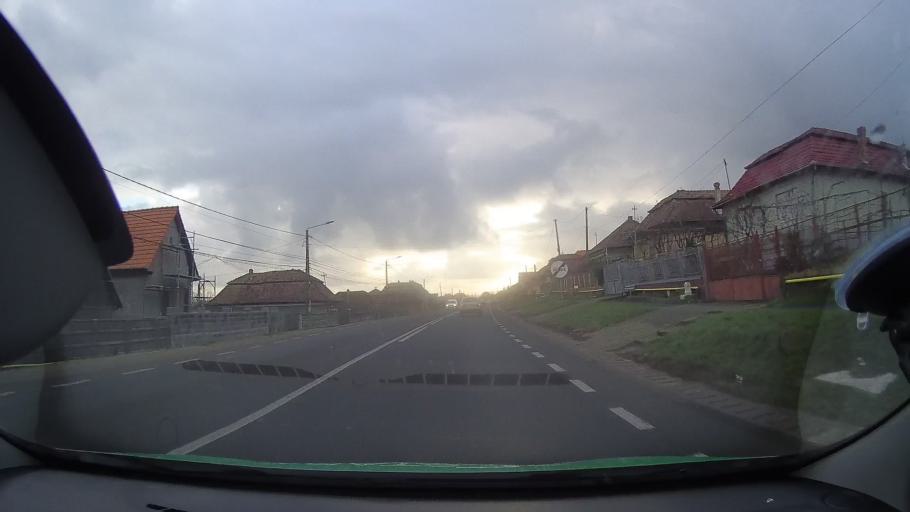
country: RO
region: Cluj
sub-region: Comuna Viisoara
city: Viisoara
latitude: 46.5084
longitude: 23.9191
